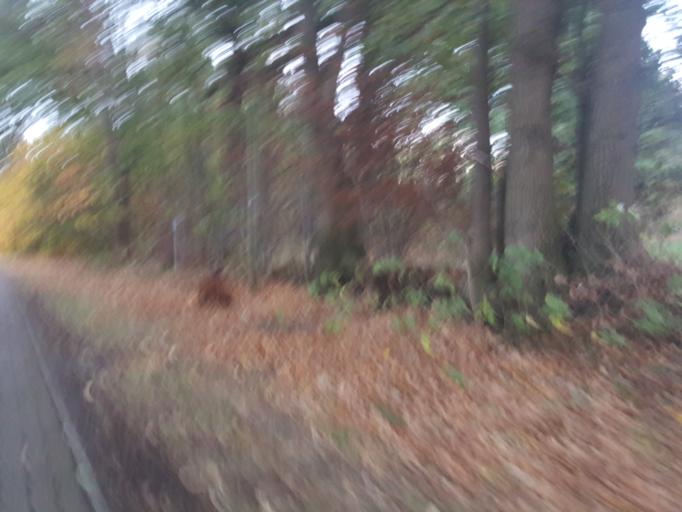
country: DE
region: Lower Saxony
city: Rastede
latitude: 53.1952
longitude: 8.1667
